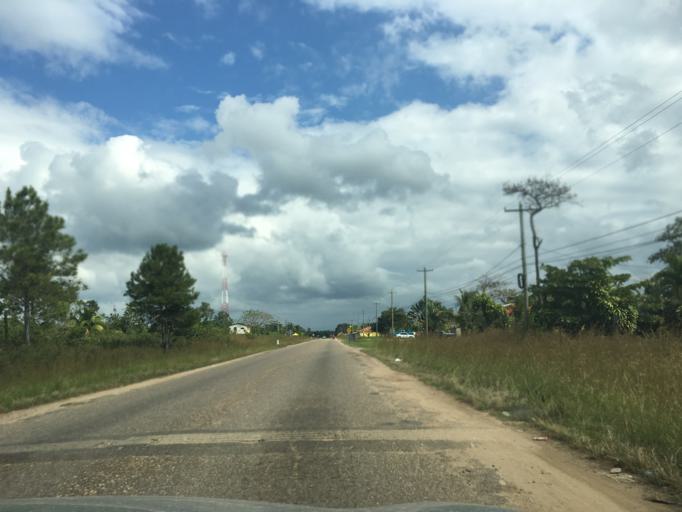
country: BZ
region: Stann Creek
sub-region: Dangriga
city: Dangriga
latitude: 16.8819
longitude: -88.3419
